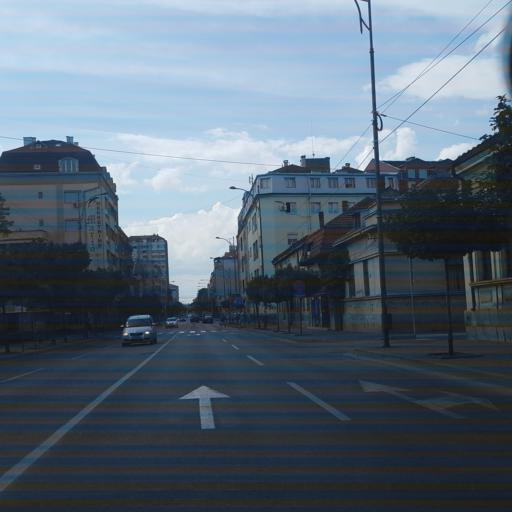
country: RS
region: Central Serbia
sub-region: Nisavski Okrug
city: Nis
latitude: 43.3207
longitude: 21.8935
